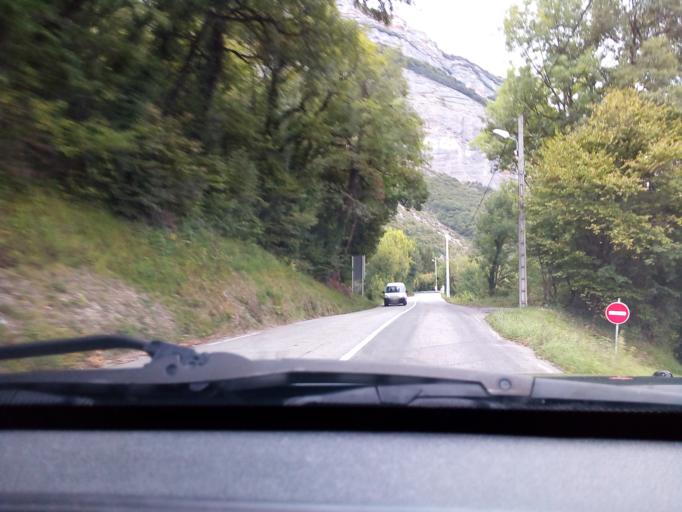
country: FR
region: Rhone-Alpes
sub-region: Departement de l'Isere
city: Corenc
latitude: 45.2250
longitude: 5.7683
